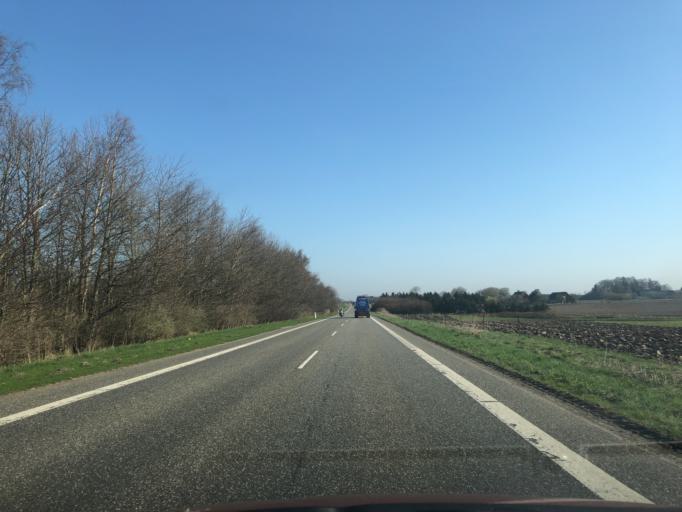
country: DK
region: Zealand
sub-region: Faxe Kommune
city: Ronnede
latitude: 55.2720
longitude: 12.0286
